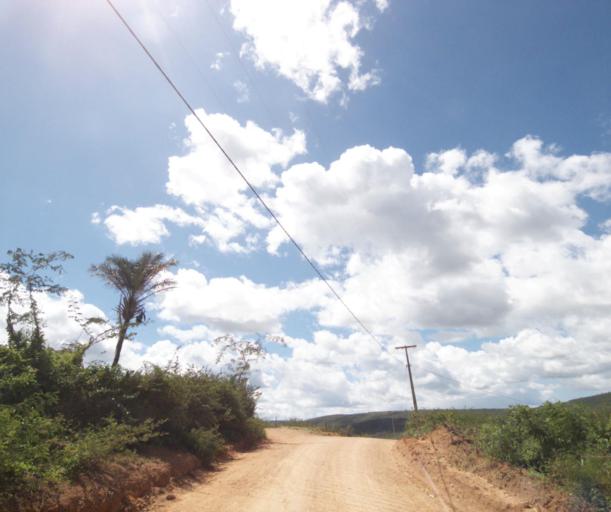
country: BR
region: Bahia
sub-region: Pocoes
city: Pocoes
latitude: -14.2993
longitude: -40.6348
